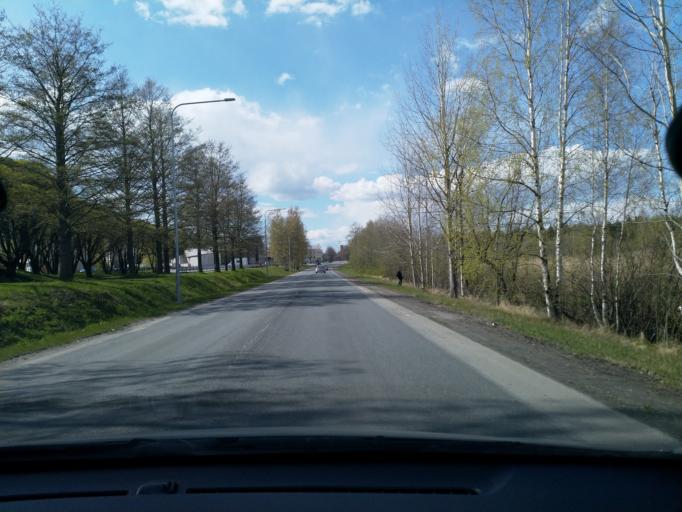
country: FI
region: Pirkanmaa
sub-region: Tampere
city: Tampere
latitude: 61.4814
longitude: 23.8078
